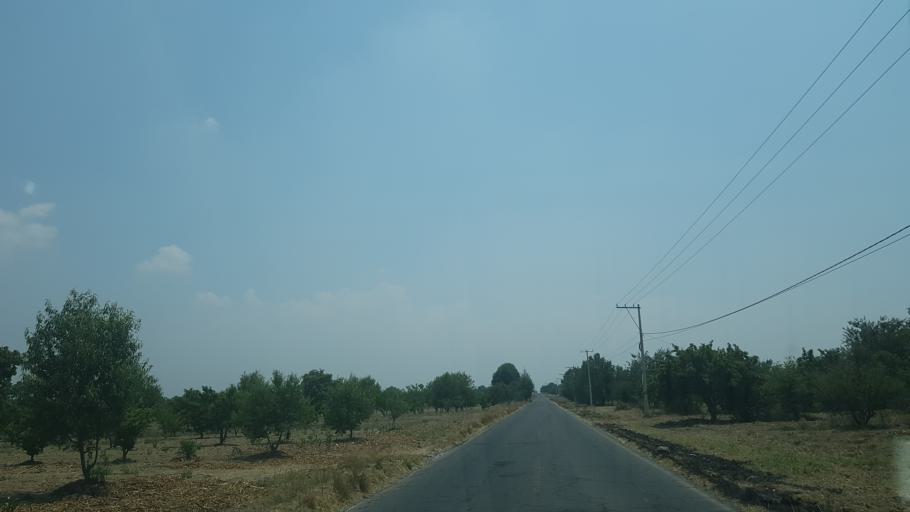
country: MX
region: Puebla
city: San Andres Calpan
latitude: 19.0989
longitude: -98.4292
